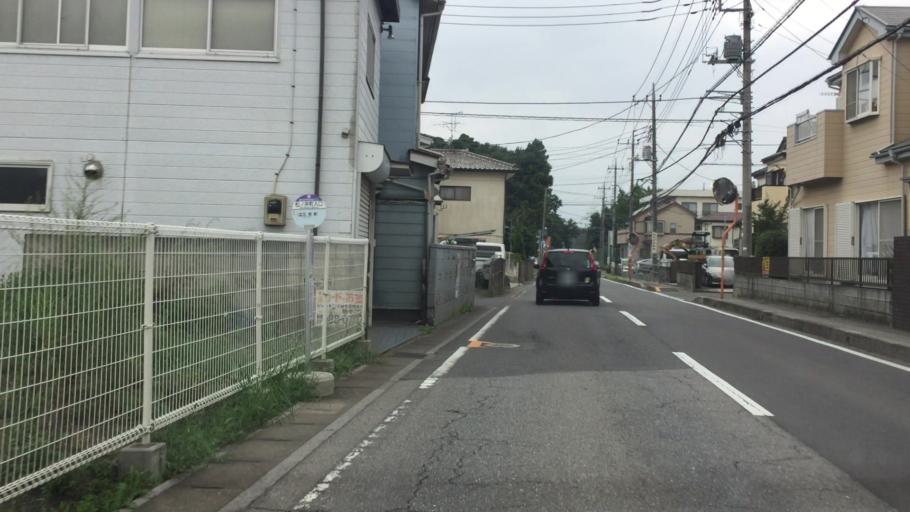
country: JP
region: Chiba
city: Kashiwa
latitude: 35.8080
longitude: 139.9667
